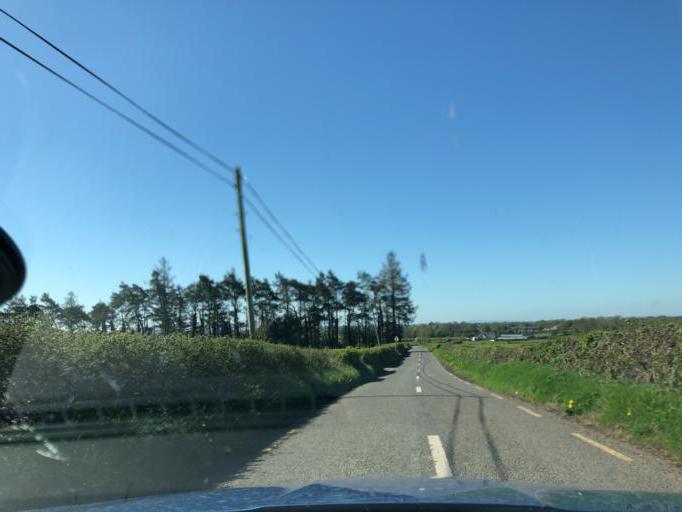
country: IE
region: Connaught
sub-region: County Galway
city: Portumna
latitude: 53.1892
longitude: -8.1636
